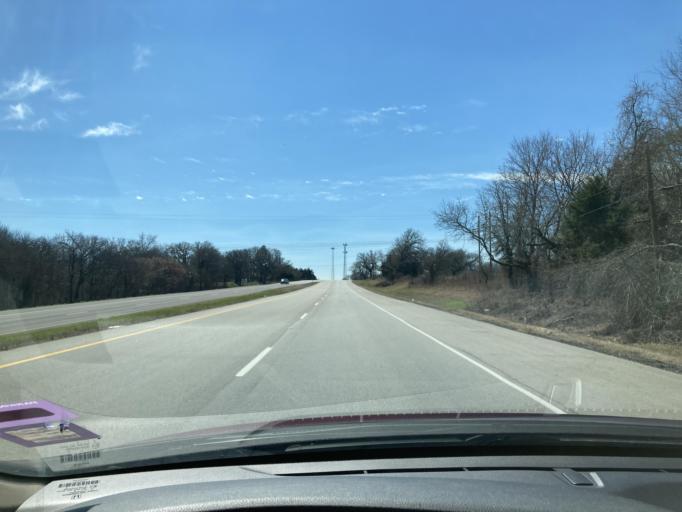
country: US
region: Texas
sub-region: Navarro County
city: Corsicana
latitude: 32.1416
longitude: -96.4682
